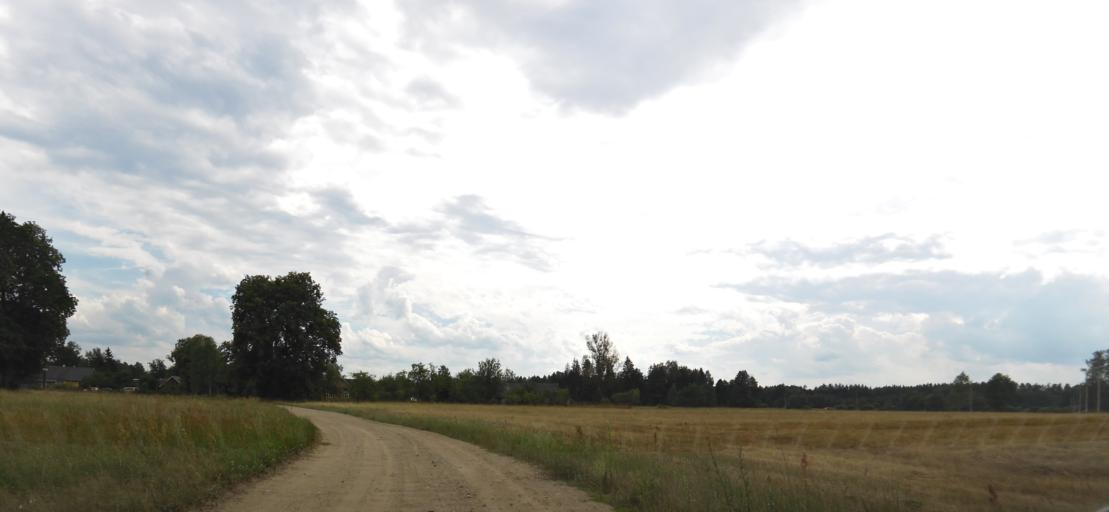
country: LT
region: Alytaus apskritis
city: Varena
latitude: 54.0223
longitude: 24.3313
